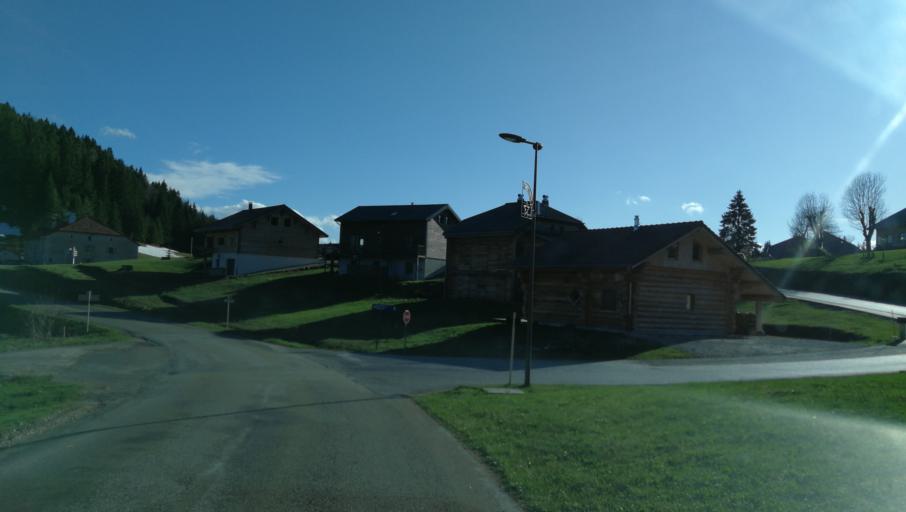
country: FR
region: Franche-Comte
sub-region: Departement du Jura
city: Saint-Claude
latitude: 46.2822
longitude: 5.8459
